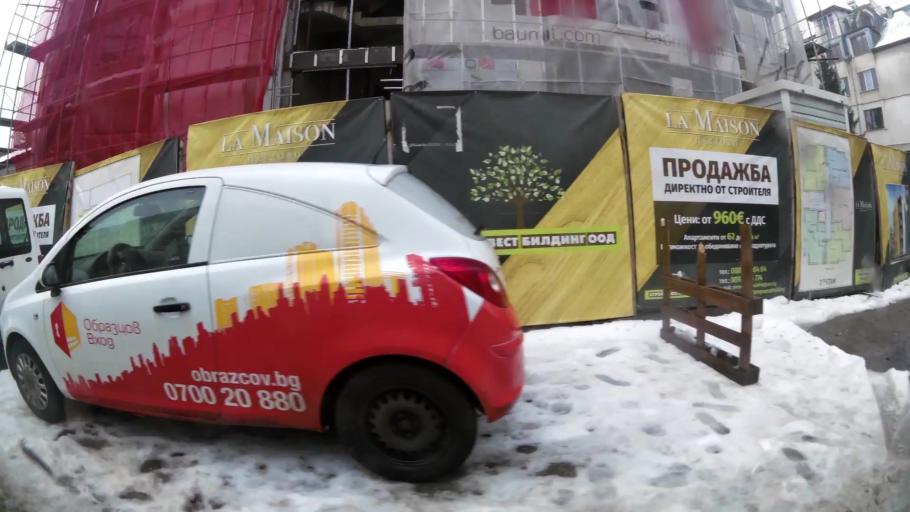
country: BG
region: Sofia-Capital
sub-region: Stolichna Obshtina
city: Sofia
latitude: 42.6609
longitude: 23.2696
